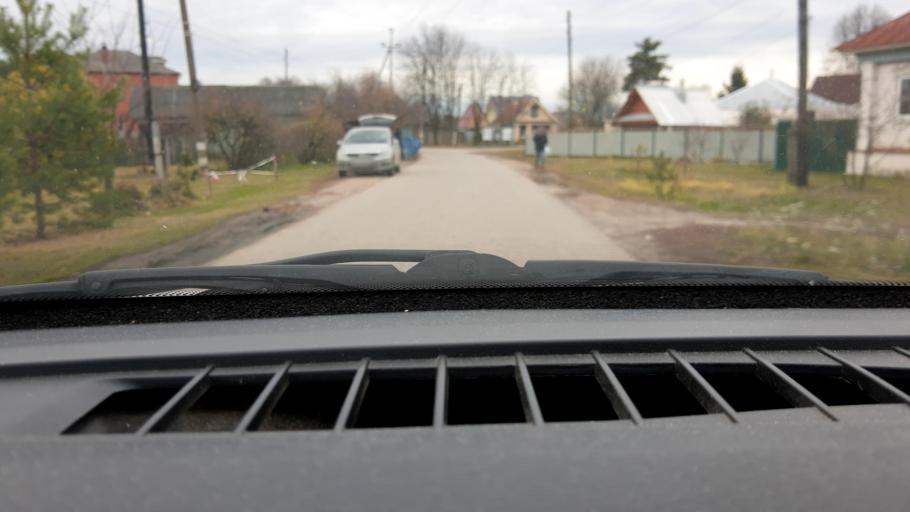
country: RU
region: Nizjnij Novgorod
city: Gorodets
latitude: 56.6396
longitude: 43.4698
